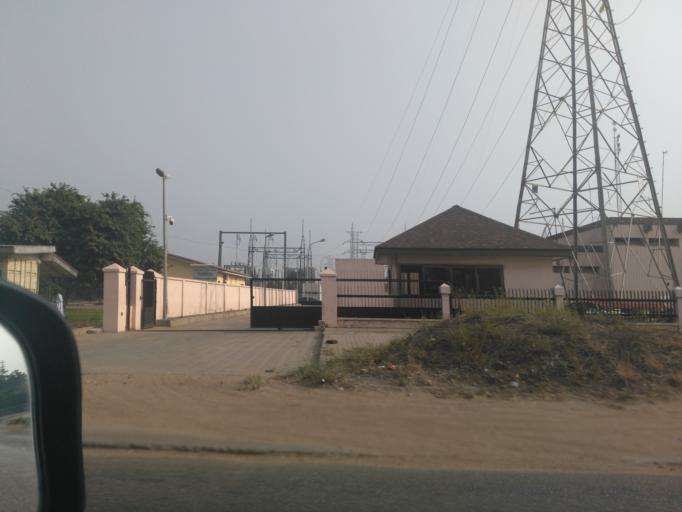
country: GH
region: Greater Accra
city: Accra
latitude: 5.6058
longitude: -0.2051
